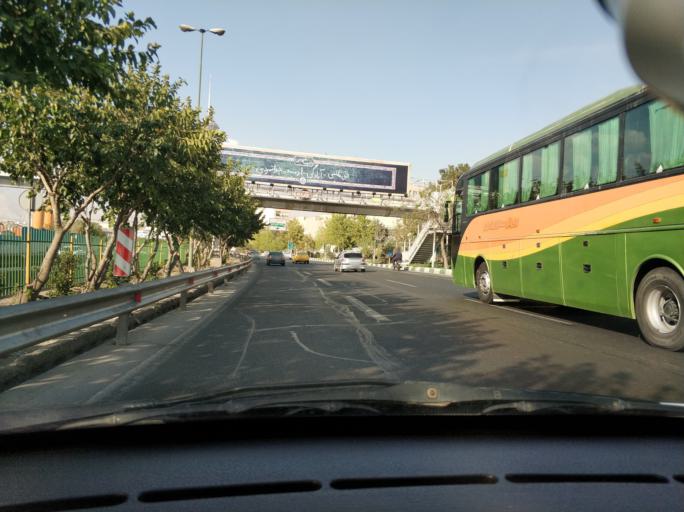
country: IR
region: Tehran
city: Tehran
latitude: 35.7310
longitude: 51.3707
